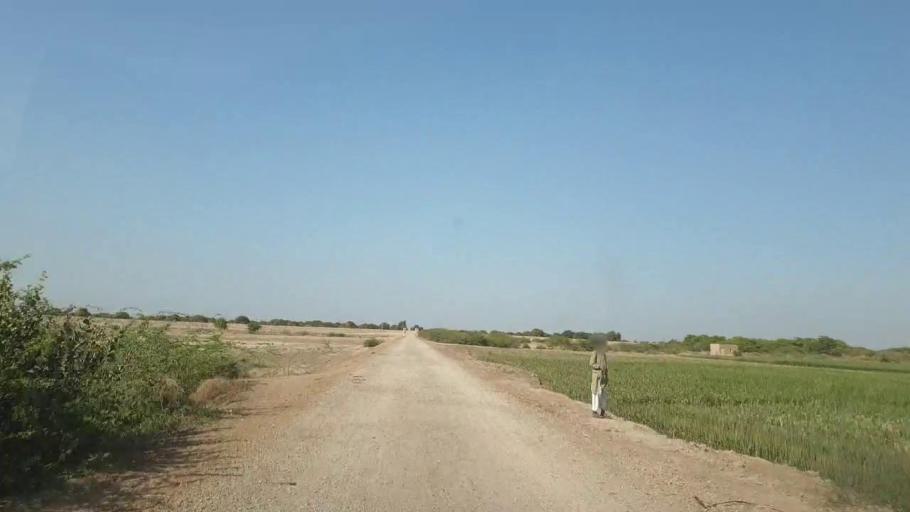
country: PK
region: Sindh
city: Nabisar
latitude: 25.0312
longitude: 69.4867
